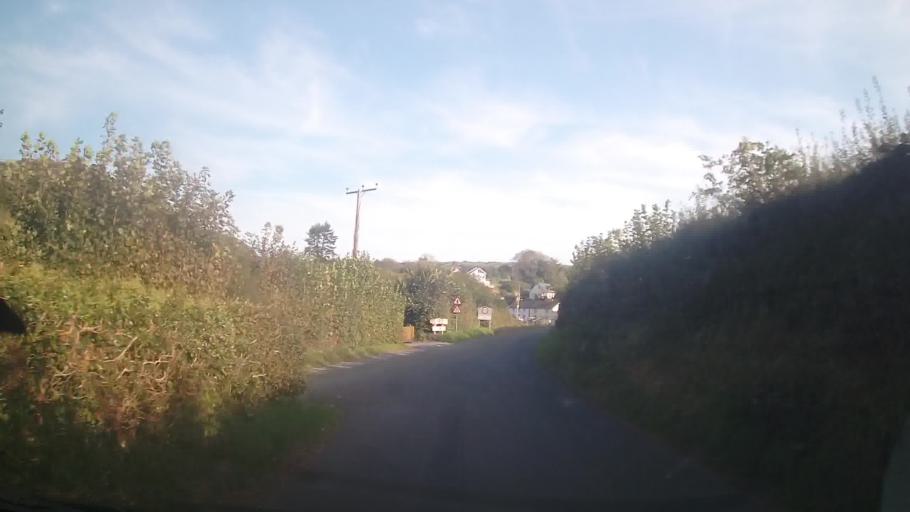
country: GB
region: Wales
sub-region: Pembrokeshire
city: Fishguard
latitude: 51.9814
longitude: -4.9345
